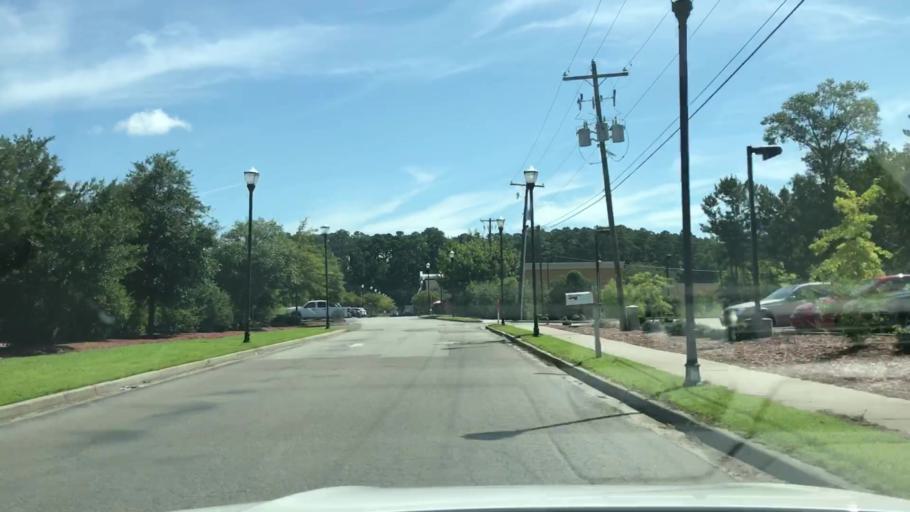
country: US
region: South Carolina
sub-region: Dorchester County
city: Summerville
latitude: 33.0113
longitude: -80.2372
